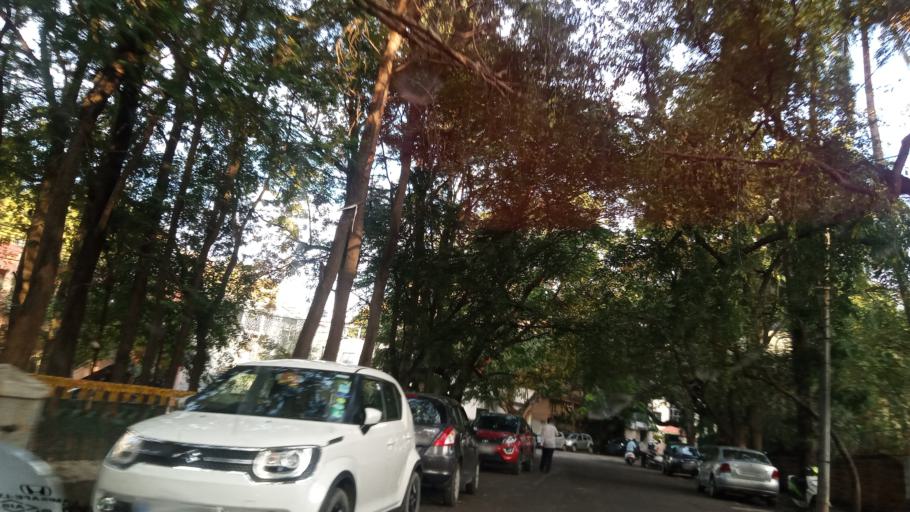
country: IN
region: Karnataka
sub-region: Bangalore Urban
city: Bangalore
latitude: 12.9343
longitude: 77.6219
